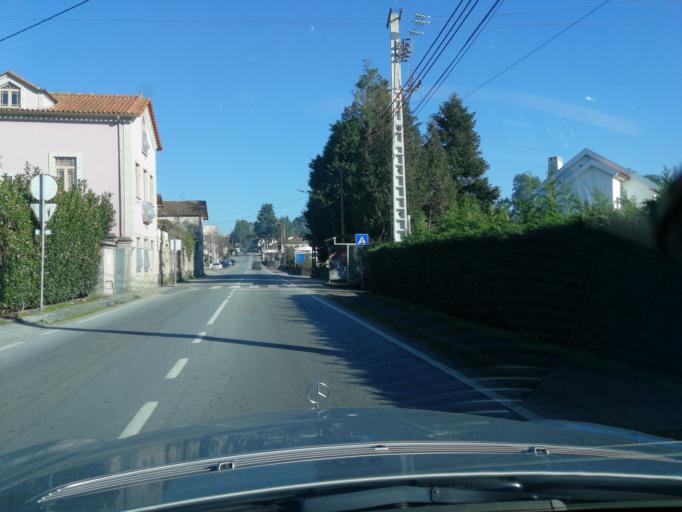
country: PT
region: Braga
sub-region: Braga
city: Adaufe
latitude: 41.6079
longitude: -8.4296
